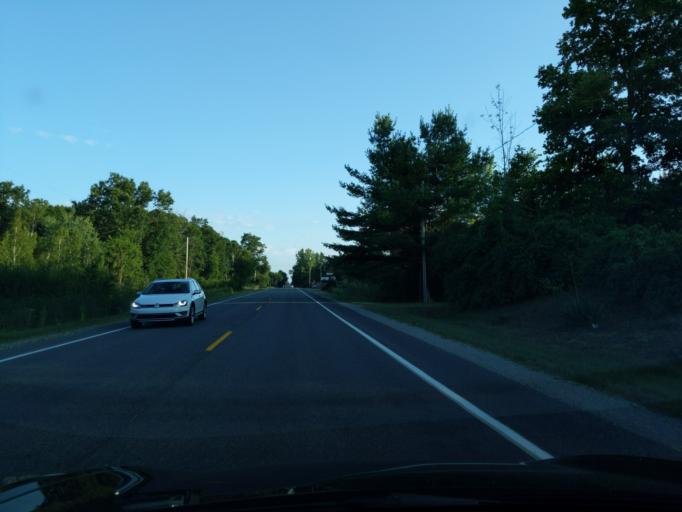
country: US
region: Michigan
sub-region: Midland County
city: Midland
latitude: 43.5619
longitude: -84.3697
